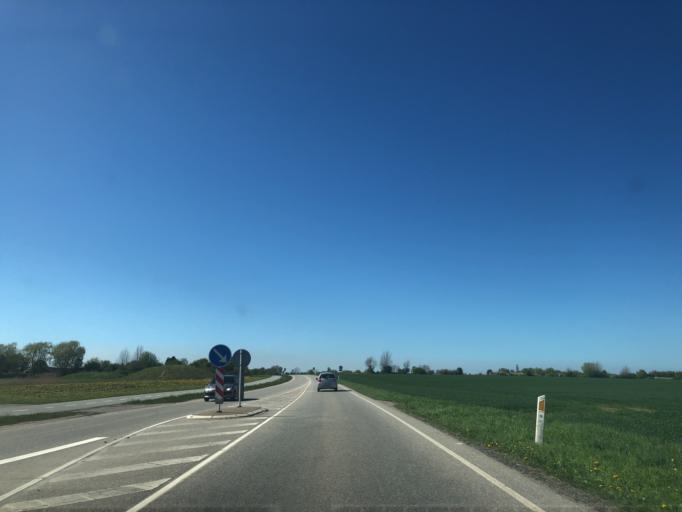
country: DK
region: Zealand
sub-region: Stevns Kommune
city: Store Heddinge
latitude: 55.3505
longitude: 12.3315
